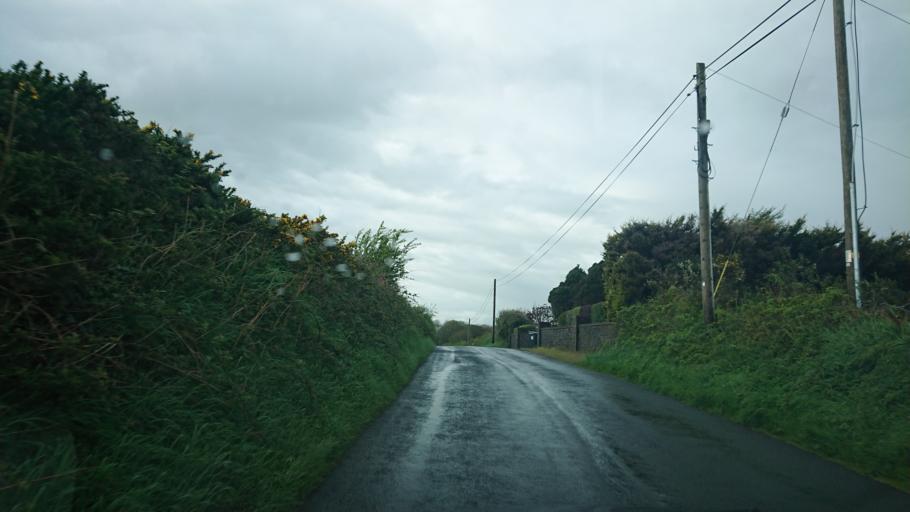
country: IE
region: Munster
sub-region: Waterford
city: Waterford
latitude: 52.2234
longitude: -7.0723
